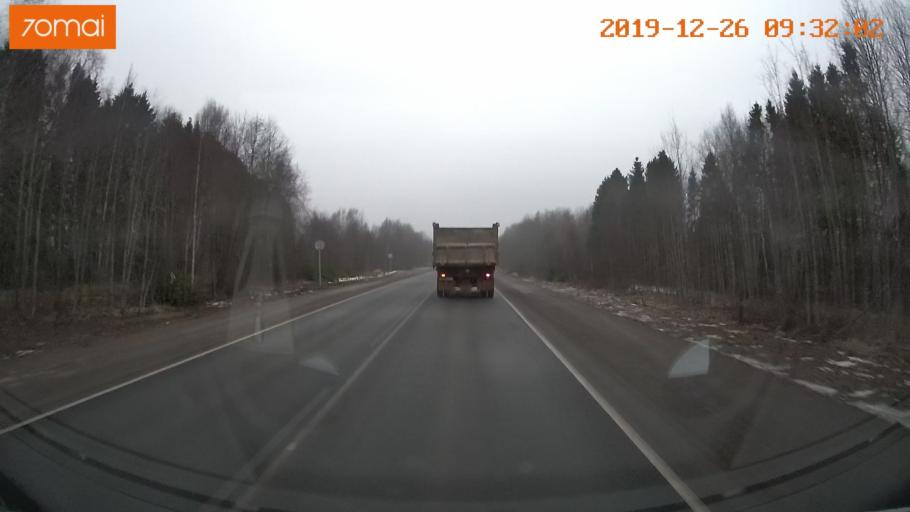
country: RU
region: Vologda
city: Gryazovets
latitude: 59.0742
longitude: 40.1213
